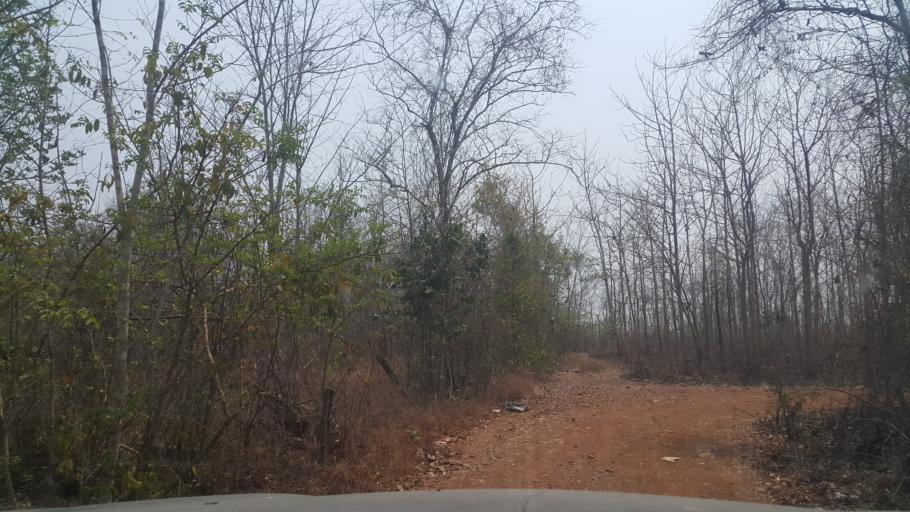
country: TH
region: Lampang
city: Sop Prap
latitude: 17.8922
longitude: 99.3200
